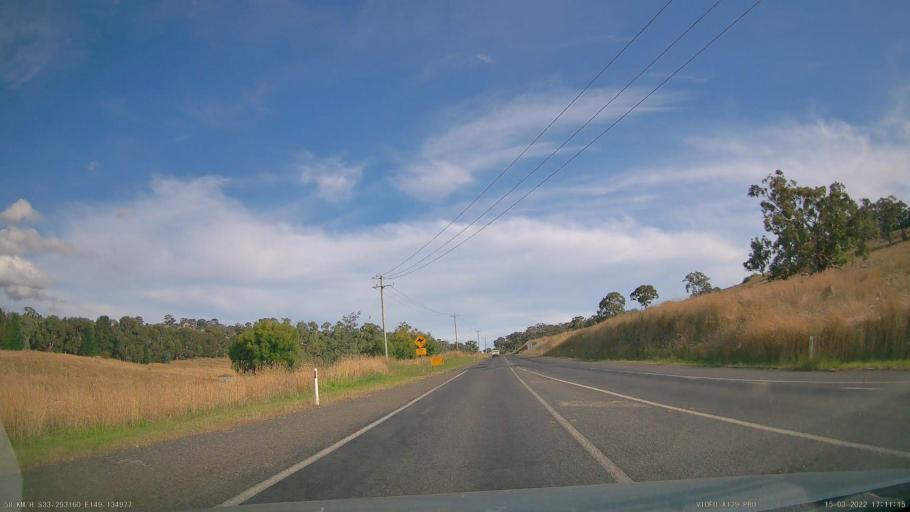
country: AU
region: New South Wales
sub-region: Orange Municipality
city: Orange
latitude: -33.2932
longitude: 149.1347
